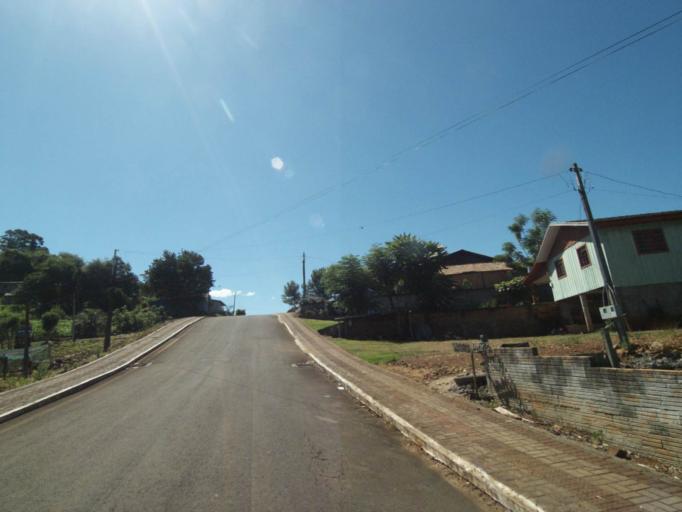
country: BR
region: Parana
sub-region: Ampere
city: Ampere
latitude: -26.1768
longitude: -53.3555
